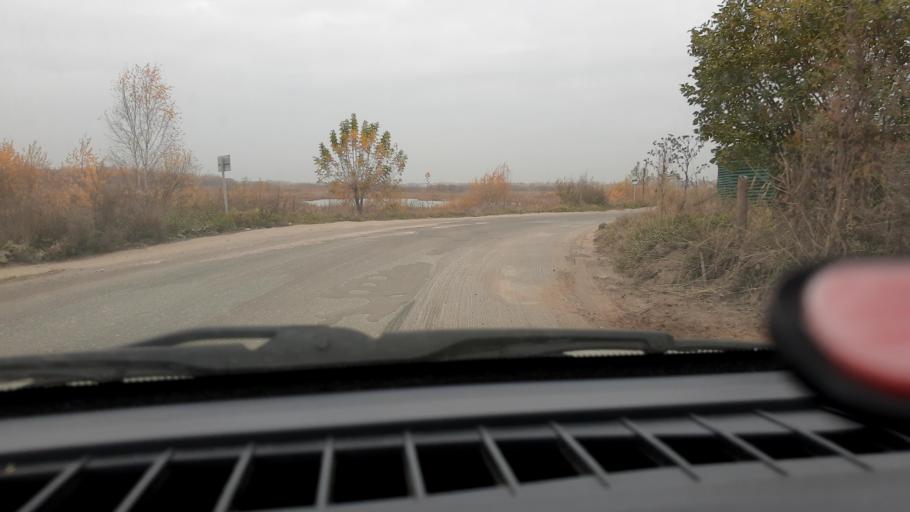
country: RU
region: Nizjnij Novgorod
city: Neklyudovo
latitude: 56.4121
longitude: 43.9749
